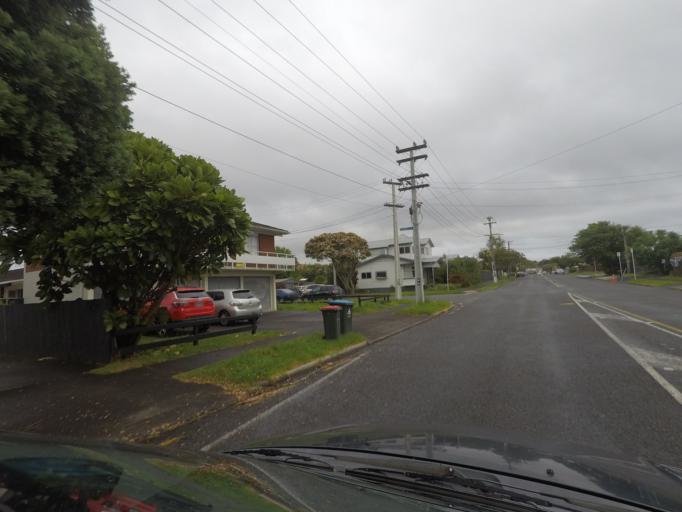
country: NZ
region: Auckland
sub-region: Auckland
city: Auckland
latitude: -36.8871
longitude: 174.7329
